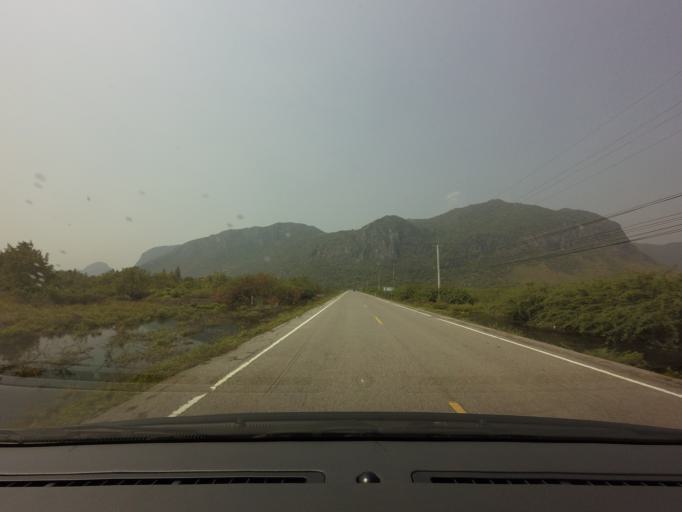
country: TH
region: Prachuap Khiri Khan
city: Sam Roi Yot
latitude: 12.1700
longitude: 99.9787
